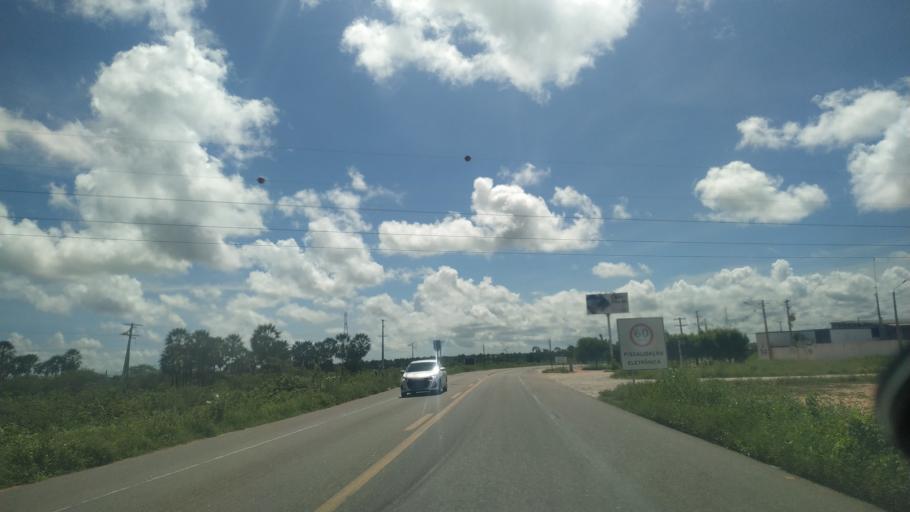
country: BR
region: Rio Grande do Norte
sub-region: Mossoro
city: Mossoro
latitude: -5.1836
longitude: -37.2991
